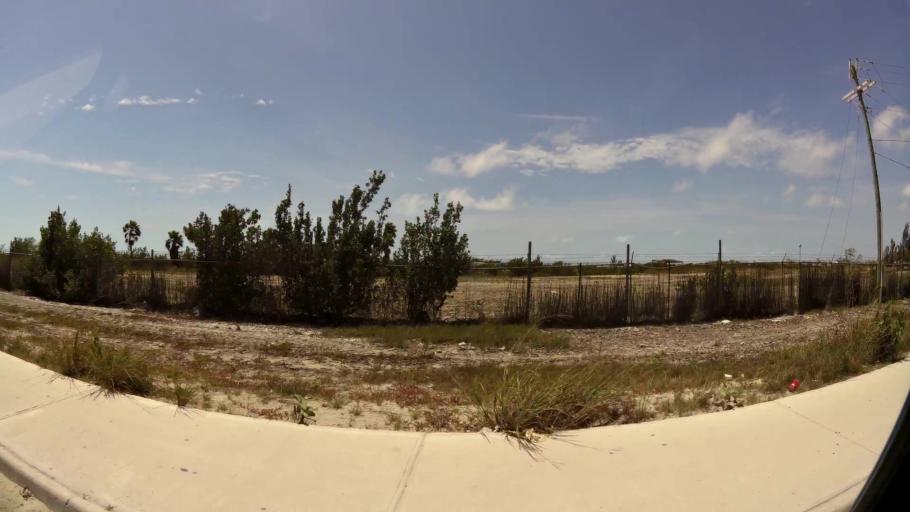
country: BS
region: Mayaguana
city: Abraham's Bay
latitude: 21.7752
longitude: -72.2537
